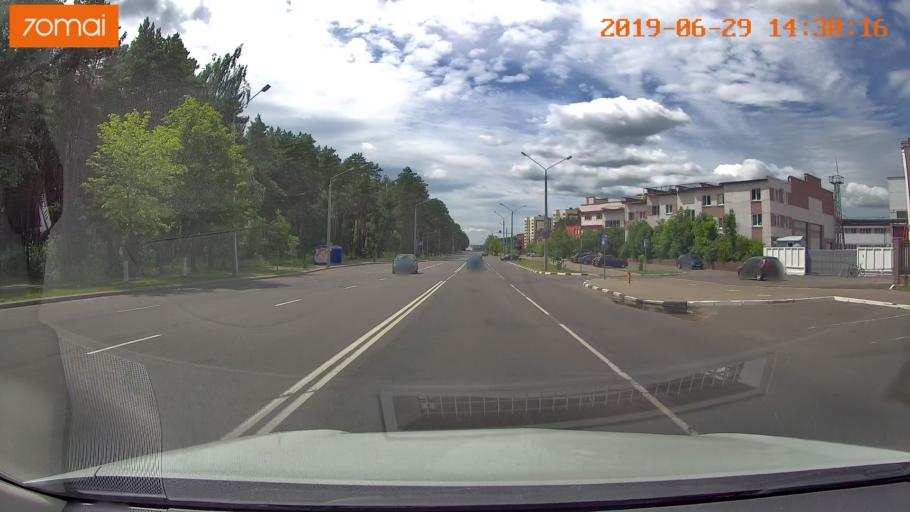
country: BY
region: Minsk
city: Salihorsk
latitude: 52.7814
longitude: 27.5197
